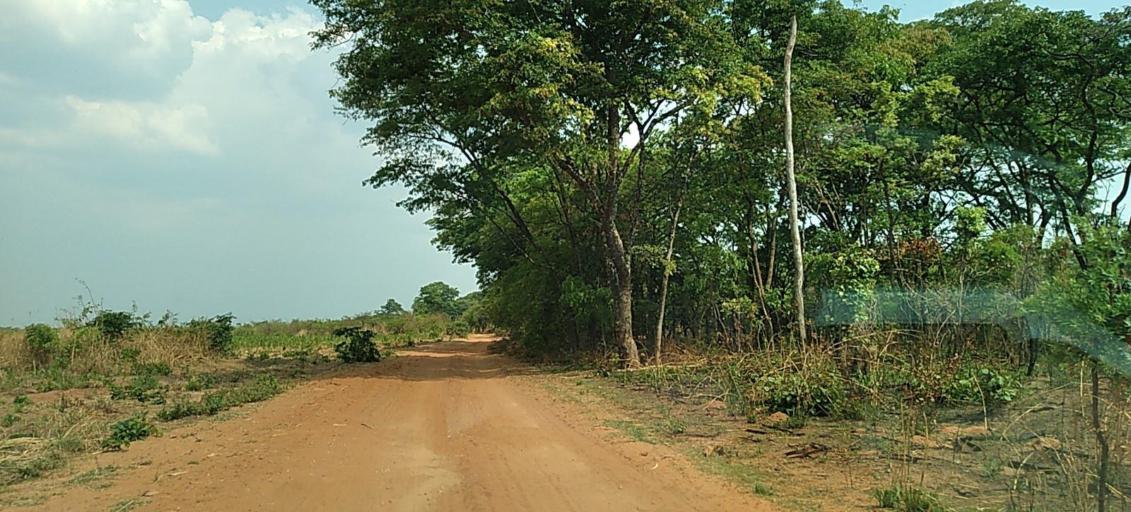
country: ZM
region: Copperbelt
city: Chingola
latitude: -12.7478
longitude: 27.7818
